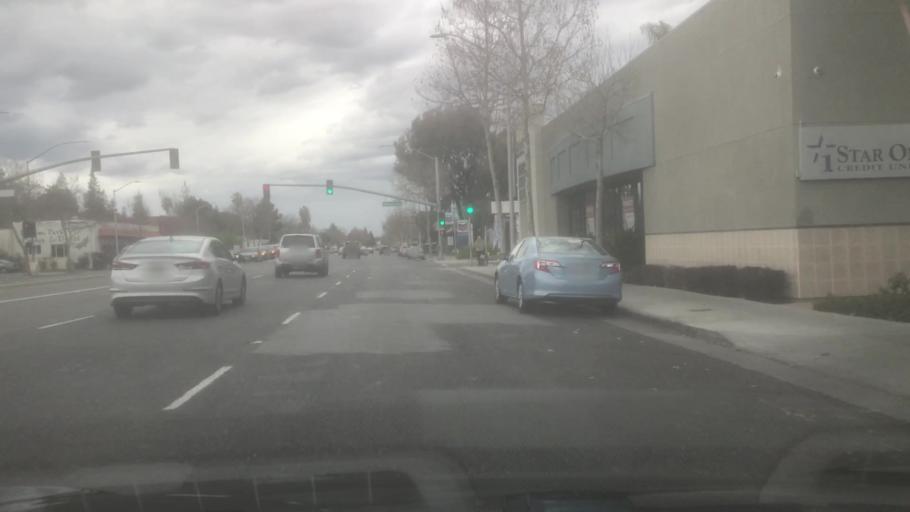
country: US
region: California
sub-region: Santa Clara County
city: Palo Alto
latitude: 37.4166
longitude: -122.1294
